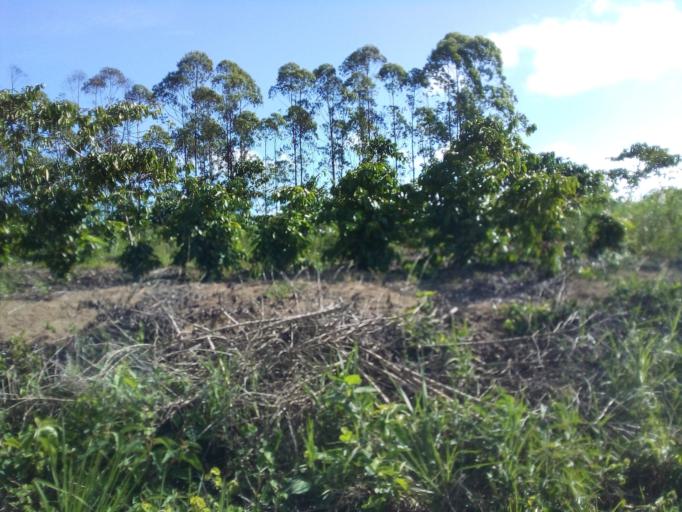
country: BR
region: Espirito Santo
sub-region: Aracruz
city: Aracruz
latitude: -19.7130
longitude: -40.2089
